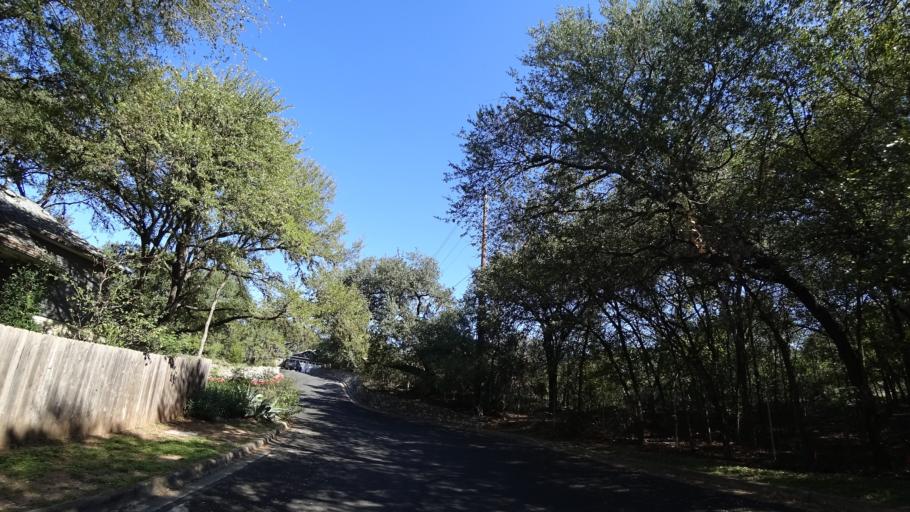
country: US
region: Texas
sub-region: Travis County
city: Austin
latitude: 30.2320
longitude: -97.7098
